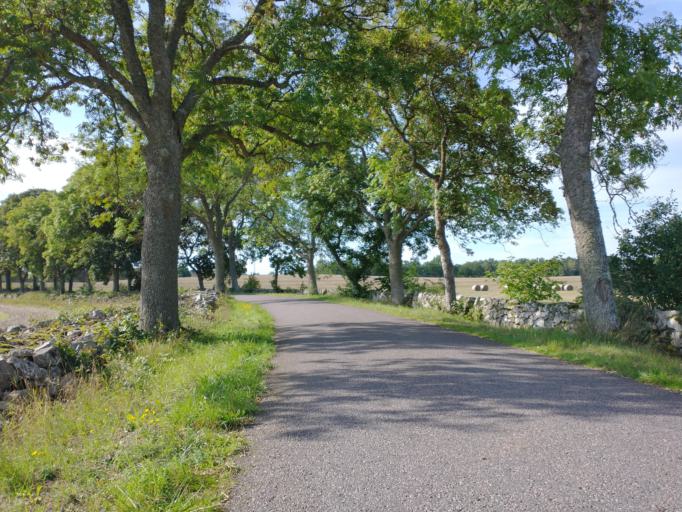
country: SE
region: Kalmar
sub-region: Kalmar Kommun
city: Lindsdal
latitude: 56.7801
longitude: 16.3208
